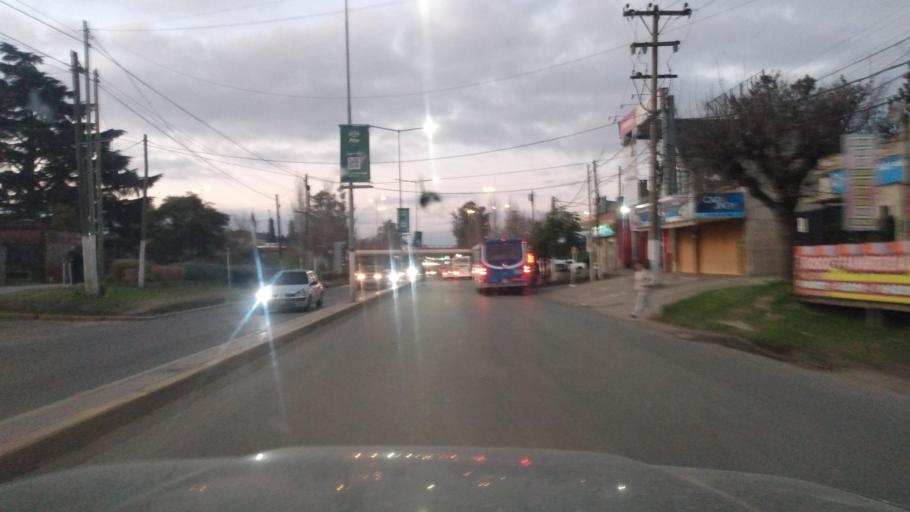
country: AR
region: Buenos Aires
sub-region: Partido de Pilar
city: Pilar
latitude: -34.4510
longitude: -58.9067
